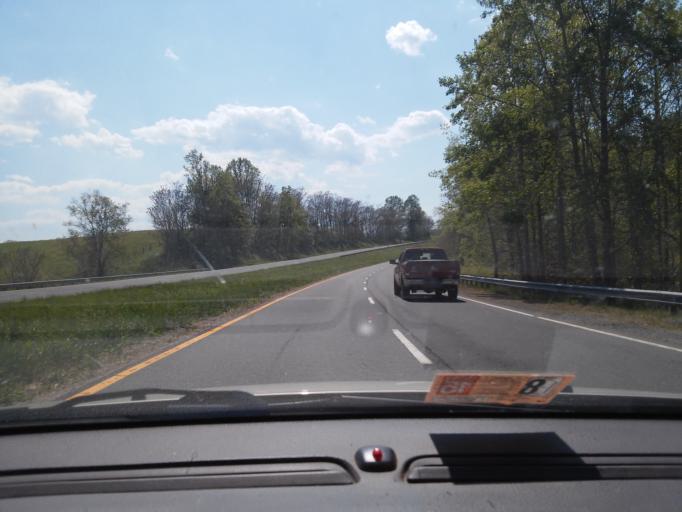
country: US
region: Virginia
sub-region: Rappahannock County
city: Washington
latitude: 38.7152
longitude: -78.1275
